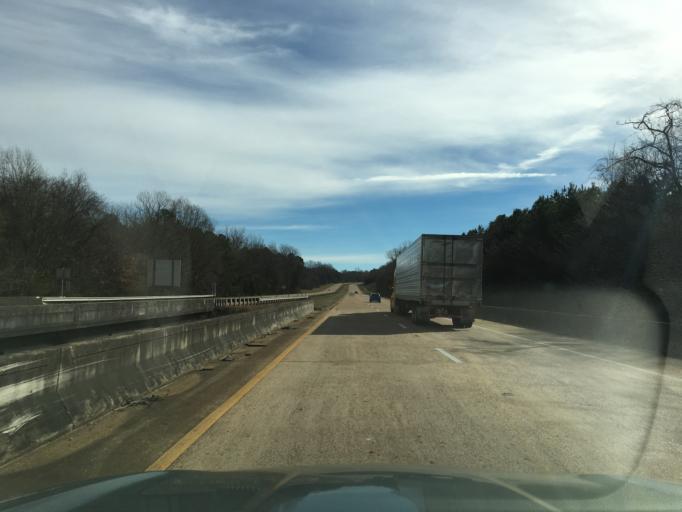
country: US
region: Mississippi
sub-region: Union County
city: New Albany
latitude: 34.4637
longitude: -88.9952
